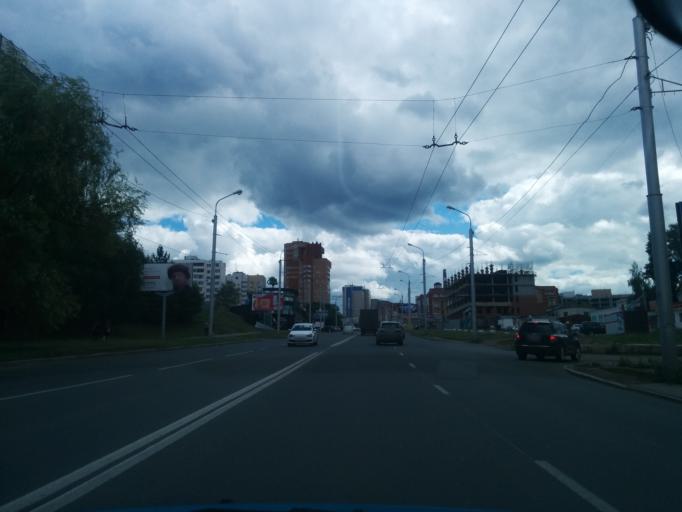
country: RU
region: Bashkortostan
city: Ufa
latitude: 54.7179
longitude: 55.9917
